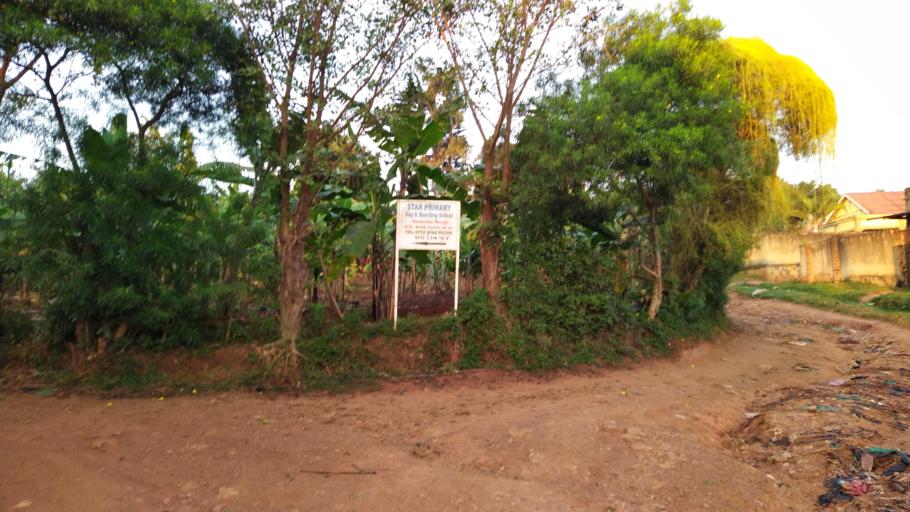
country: UG
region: Central Region
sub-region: Kampala District
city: Kampala
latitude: 0.2708
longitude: 32.5749
